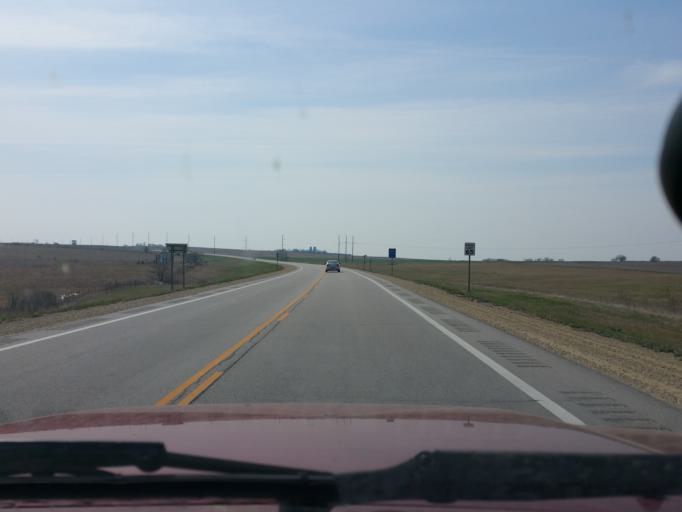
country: US
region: Kansas
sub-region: Riley County
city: Ogden
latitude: 39.2960
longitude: -96.7553
